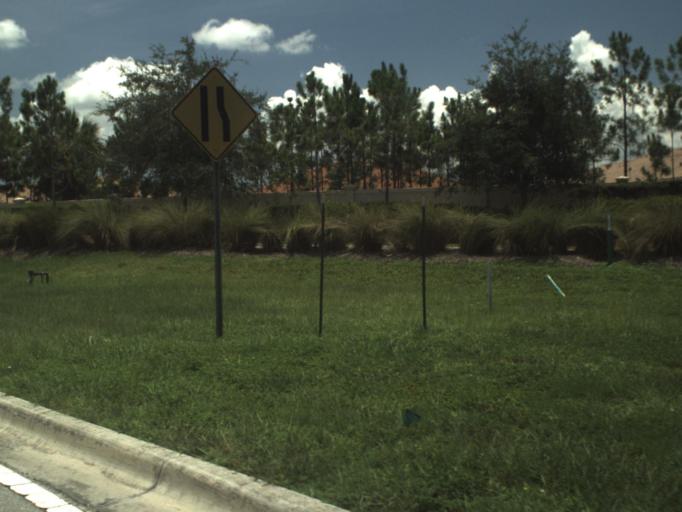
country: US
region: Florida
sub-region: Martin County
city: Palm City
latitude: 27.1155
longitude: -80.2535
